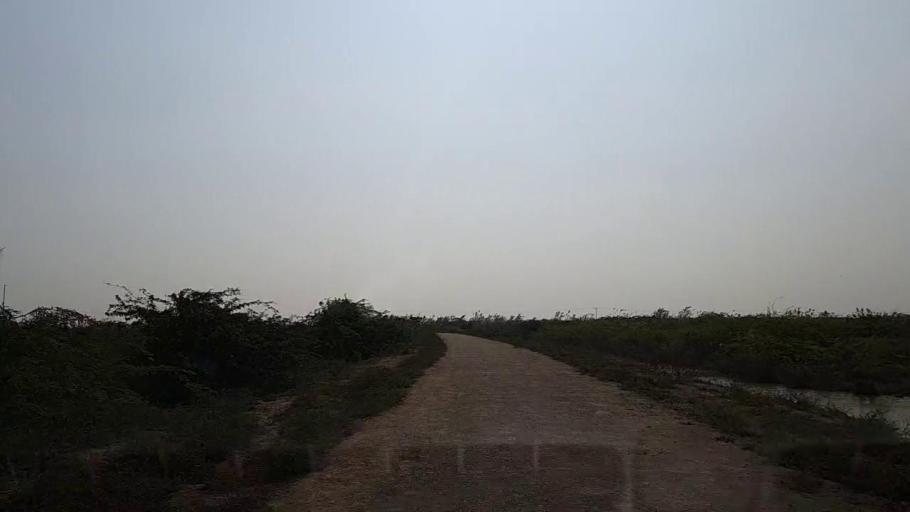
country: PK
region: Sindh
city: Mirpur Sakro
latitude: 24.6526
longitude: 67.6905
